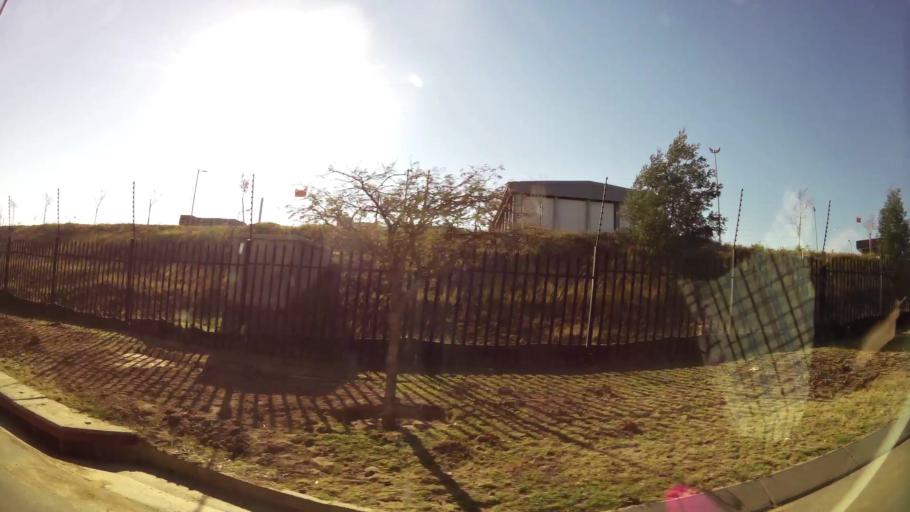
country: ZA
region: Gauteng
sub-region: City of Johannesburg Metropolitan Municipality
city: Modderfontein
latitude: -26.0526
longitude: 28.1655
